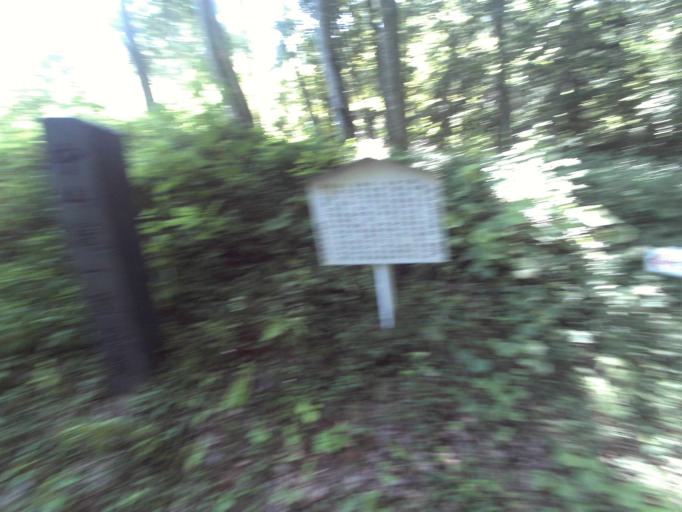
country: JP
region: Nagano
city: Komoro
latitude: 36.2664
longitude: 138.3697
